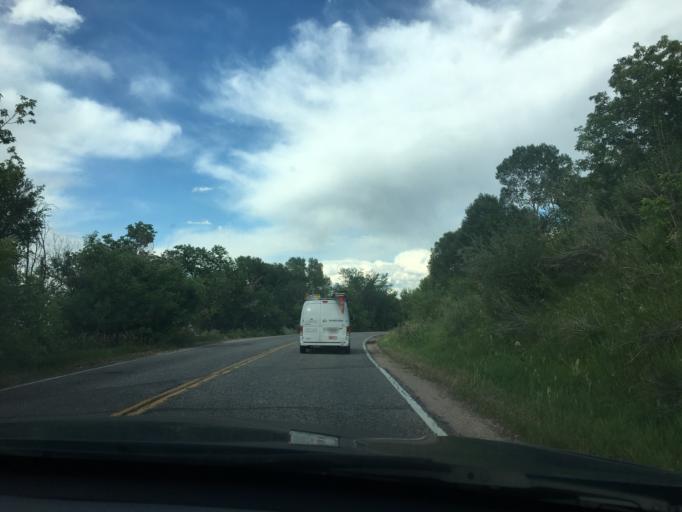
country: US
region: Colorado
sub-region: Jefferson County
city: Applewood
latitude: 39.7663
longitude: -105.1905
